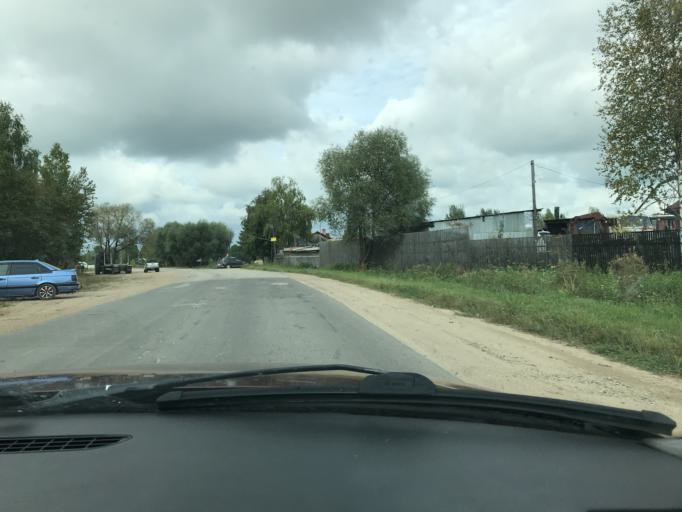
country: RU
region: Kaluga
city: Maloyaroslavets
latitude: 54.9850
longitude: 36.4716
